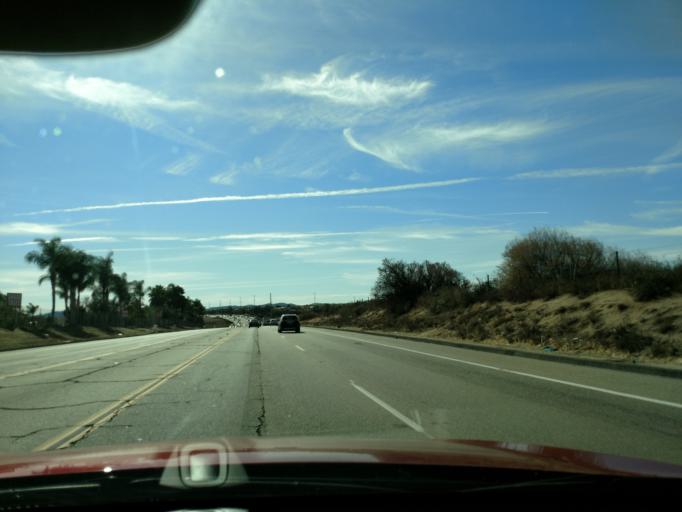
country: US
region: California
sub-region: Riverside County
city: Murrieta Hot Springs
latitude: 33.5879
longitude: -117.1288
